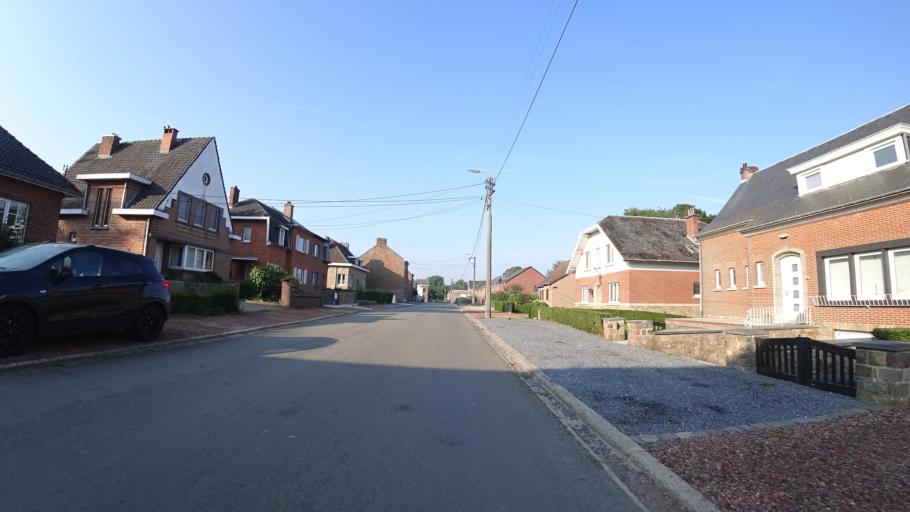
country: BE
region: Wallonia
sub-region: Province de Namur
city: Namur
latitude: 50.4988
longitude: 4.8007
